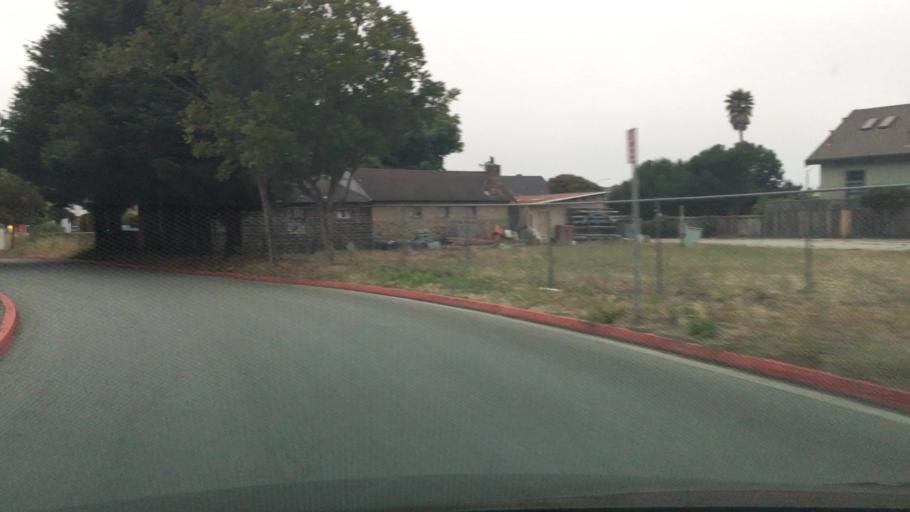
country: US
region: California
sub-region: San Mateo County
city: Half Moon Bay
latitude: 37.4670
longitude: -122.4282
